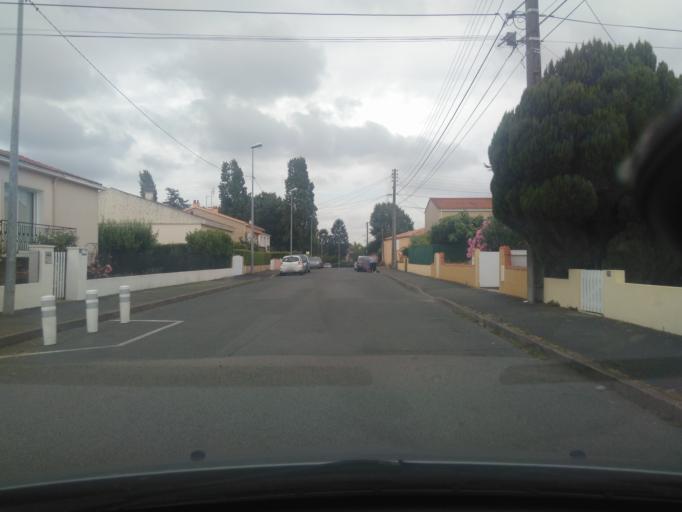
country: FR
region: Pays de la Loire
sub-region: Departement de la Vendee
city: La Roche-sur-Yon
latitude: 46.6637
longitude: -1.4035
